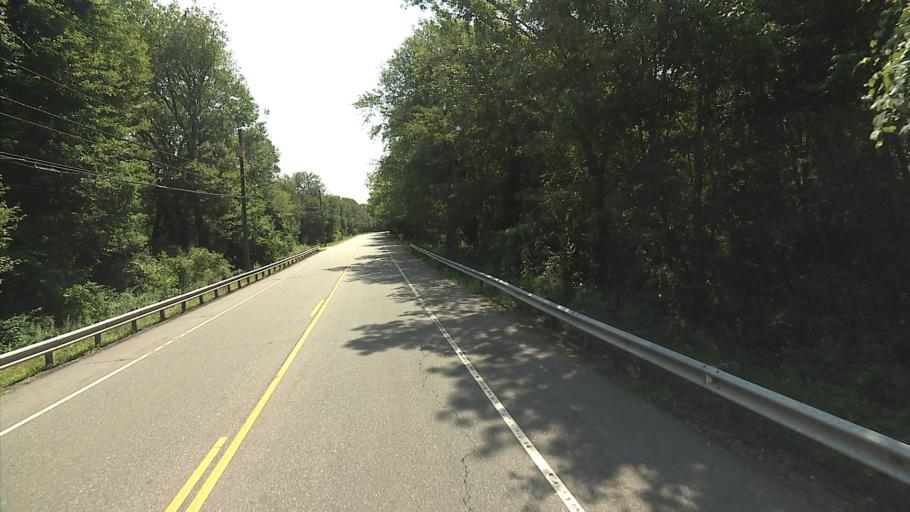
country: US
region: Connecticut
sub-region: New London County
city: Colchester
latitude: 41.5536
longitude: -72.2837
